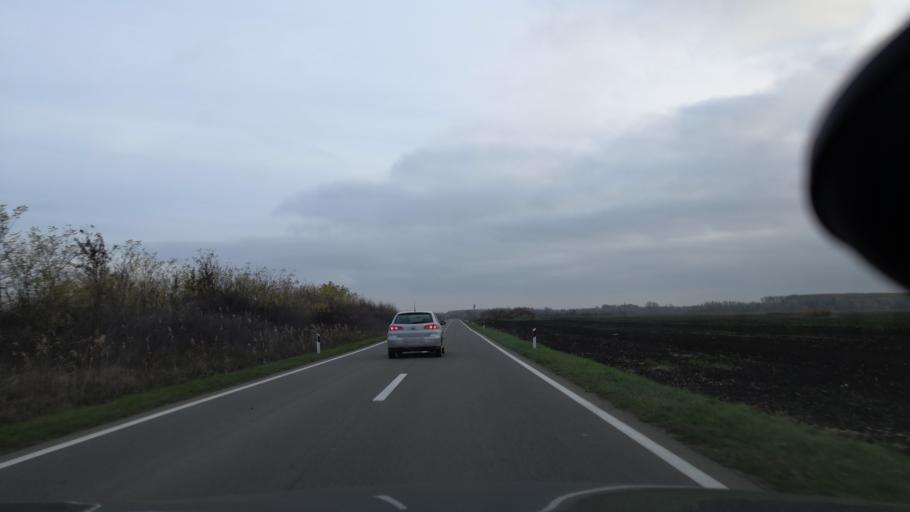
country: RS
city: Sanad
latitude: 46.0037
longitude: 20.1014
